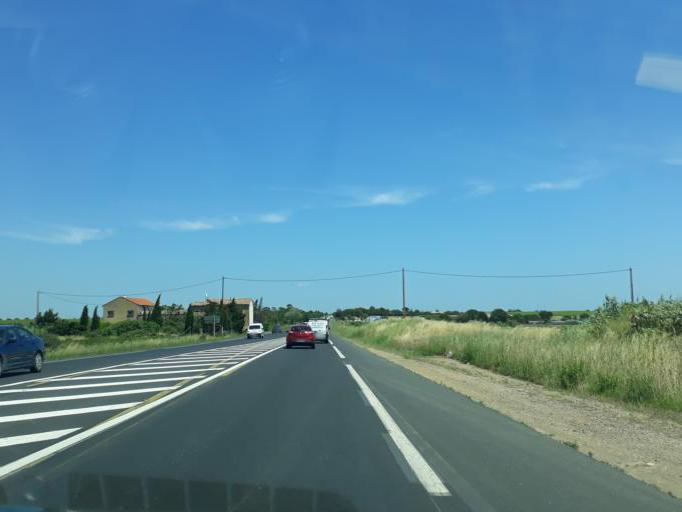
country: FR
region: Languedoc-Roussillon
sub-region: Departement de l'Herault
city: Portiragnes
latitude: 43.3142
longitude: 3.3630
